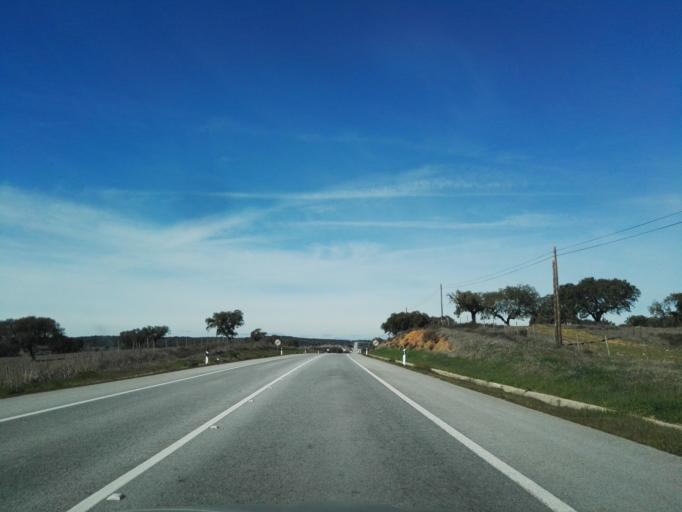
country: PT
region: Portalegre
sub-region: Arronches
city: Arronches
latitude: 39.1509
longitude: -7.3108
